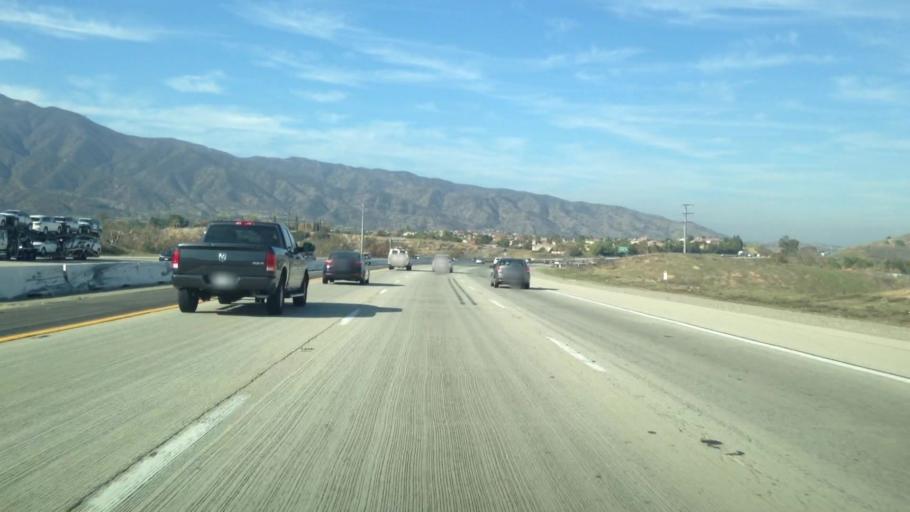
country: US
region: California
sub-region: Riverside County
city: El Cerrito
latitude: 33.7609
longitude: -117.4687
